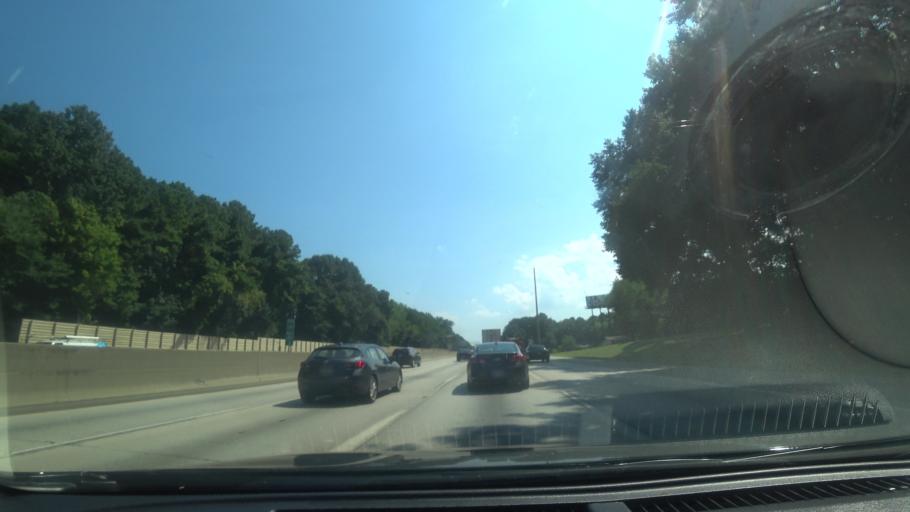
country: US
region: Georgia
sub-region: DeKalb County
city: Avondale Estates
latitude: 33.7628
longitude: -84.2326
